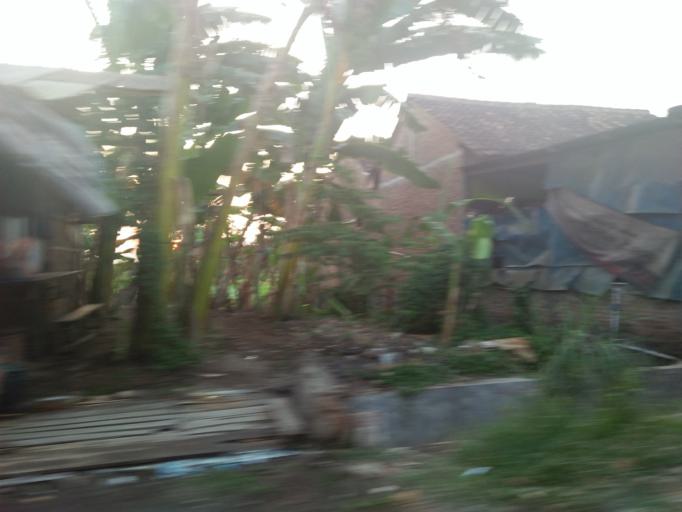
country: ID
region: Daerah Istimewa Yogyakarta
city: Sewon
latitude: -7.8508
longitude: 110.4099
